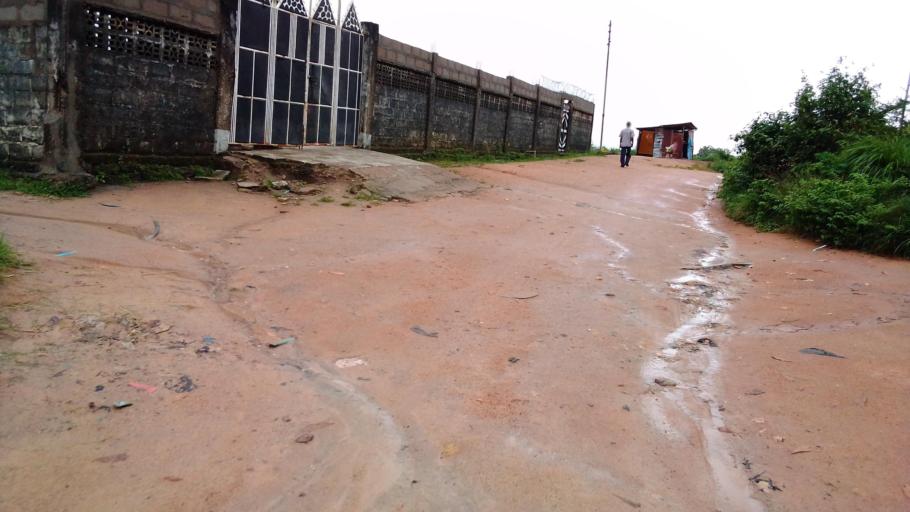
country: SL
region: Eastern Province
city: Kenema
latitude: 7.8984
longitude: -11.1837
